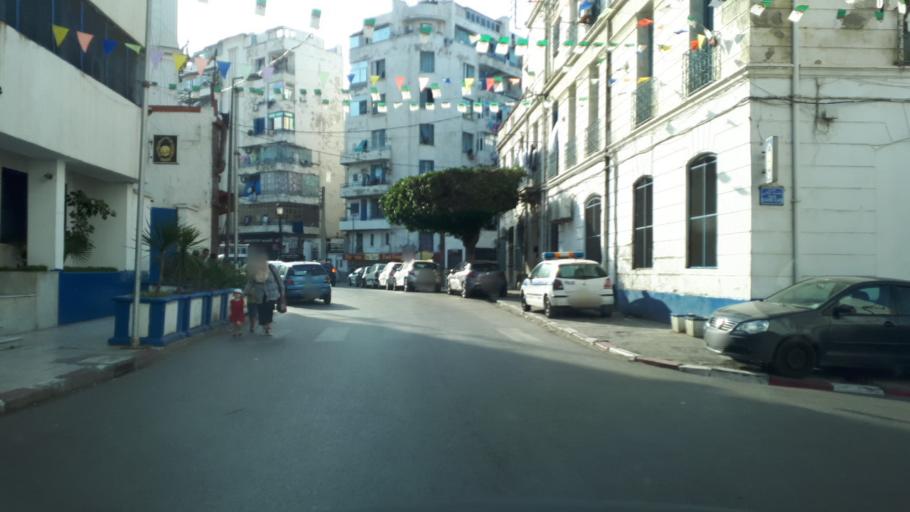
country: DZ
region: Alger
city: Algiers
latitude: 36.7918
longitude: 3.0533
